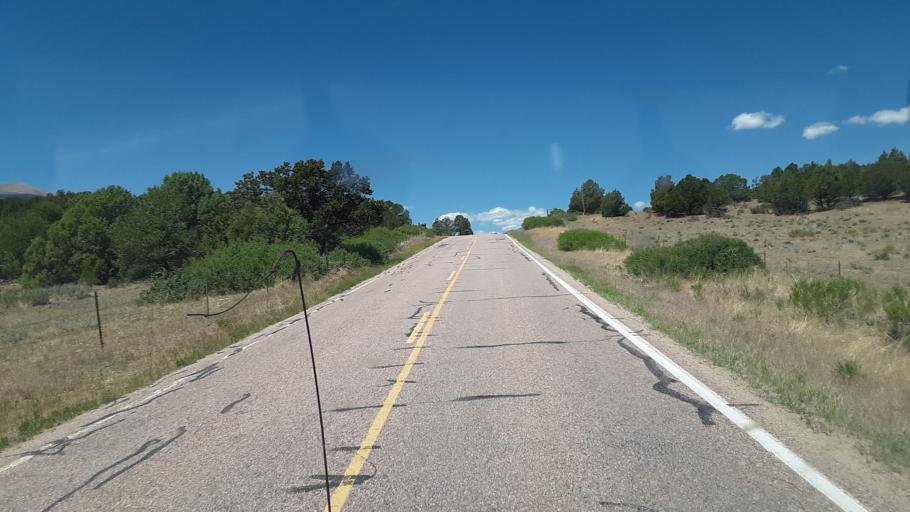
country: US
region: Colorado
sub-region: Custer County
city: Westcliffe
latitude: 38.3092
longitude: -105.6373
